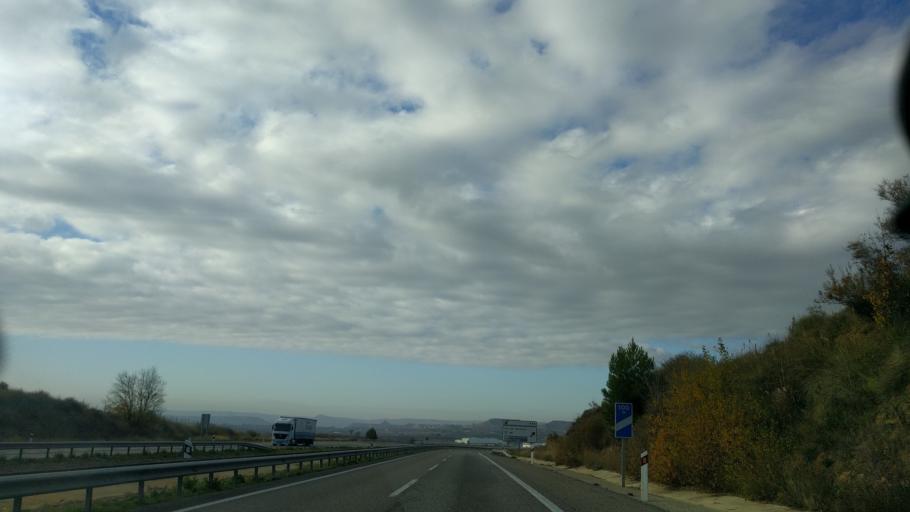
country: ES
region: Catalonia
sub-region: Provincia de Lleida
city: Soses
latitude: 41.5381
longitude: 0.4473
